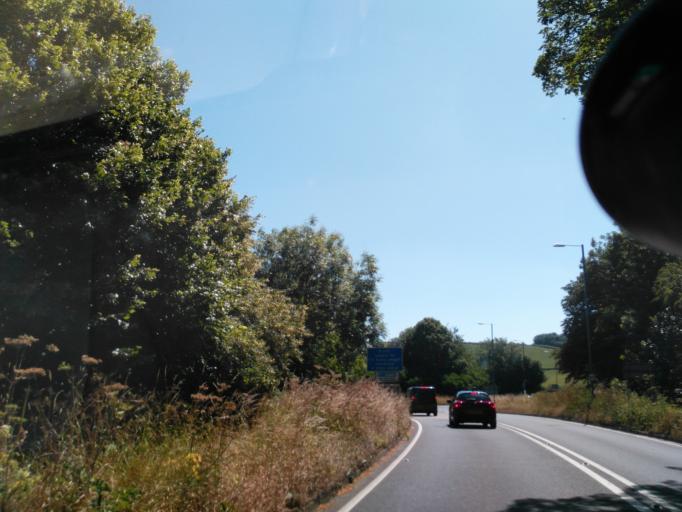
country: GB
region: England
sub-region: Bath and North East Somerset
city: Corston
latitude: 51.3869
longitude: -2.4317
